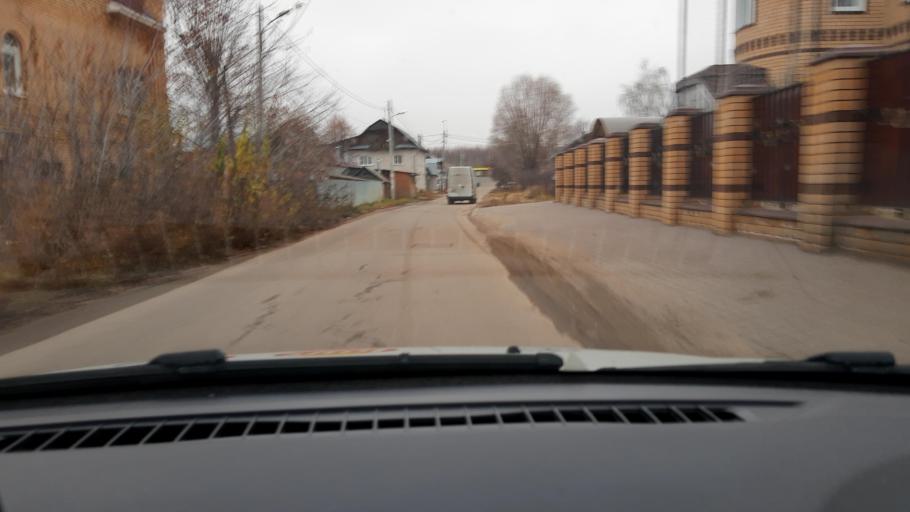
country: RU
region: Nizjnij Novgorod
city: Burevestnik
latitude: 56.2035
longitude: 43.7785
